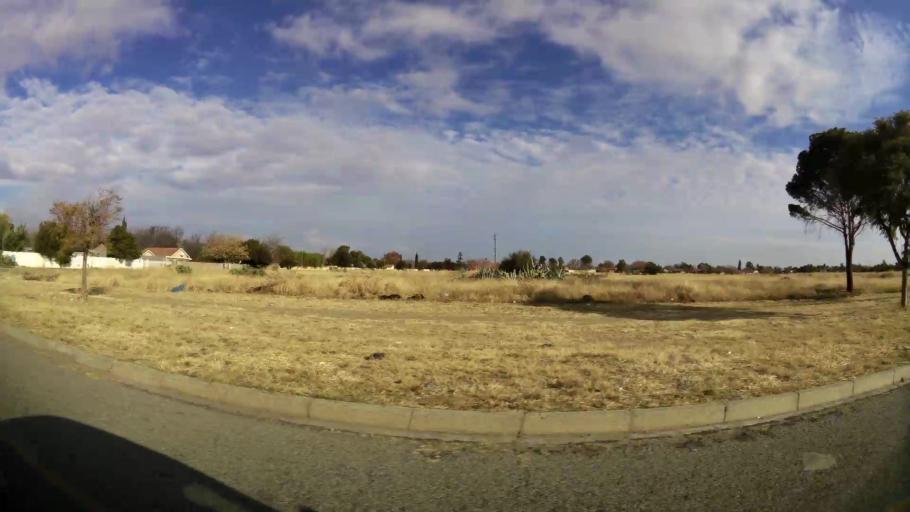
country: ZA
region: Orange Free State
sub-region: Lejweleputswa District Municipality
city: Welkom
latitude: -27.9747
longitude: 26.7044
